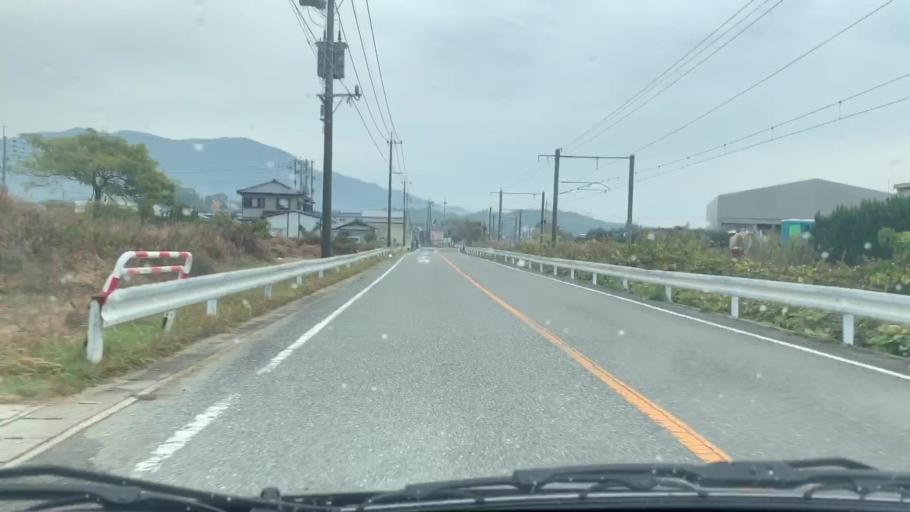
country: JP
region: Saga Prefecture
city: Takeocho-takeo
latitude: 33.2159
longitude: 130.0708
